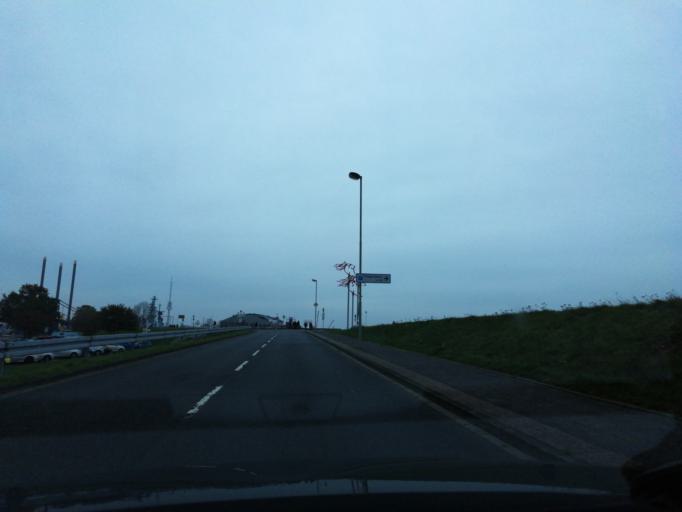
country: DE
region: Lower Saxony
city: Wilhelmshaven
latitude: 53.5114
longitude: 8.1326
